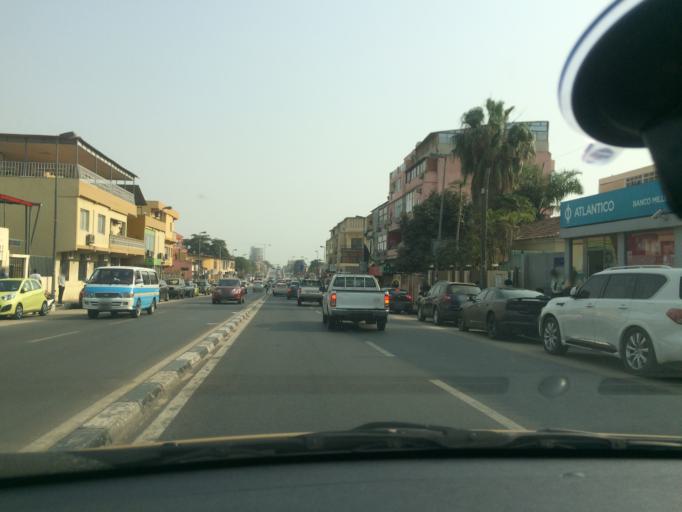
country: AO
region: Luanda
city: Luanda
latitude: -8.8277
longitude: 13.2226
